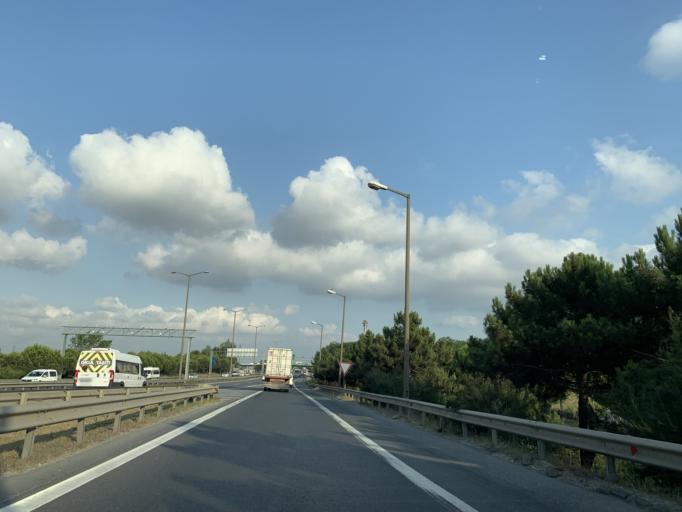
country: TR
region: Istanbul
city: Esenyurt
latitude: 41.0525
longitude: 28.6839
